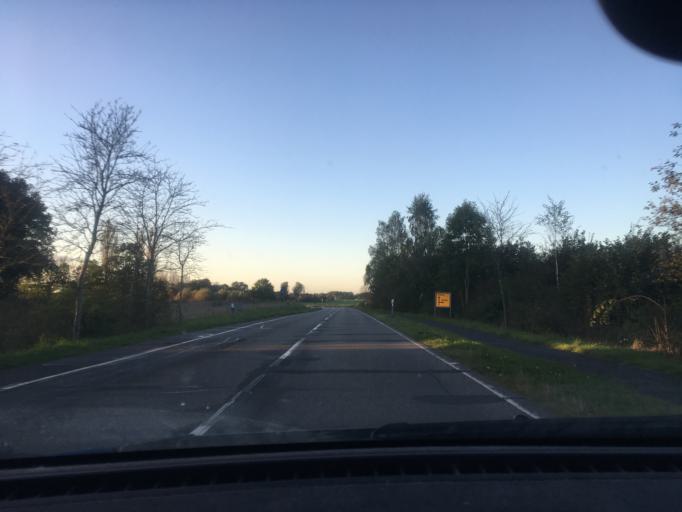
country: DE
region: Lower Saxony
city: Wendisch Evern
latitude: 53.2186
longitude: 10.4640
